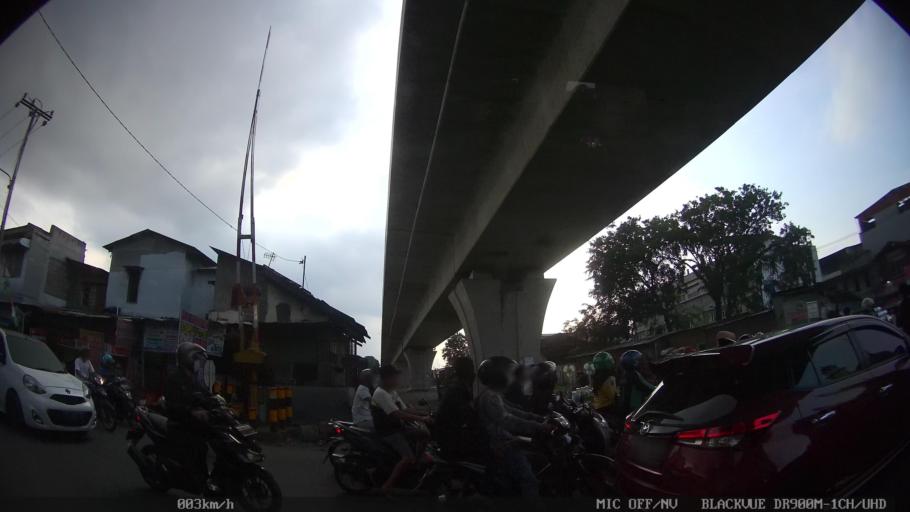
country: ID
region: North Sumatra
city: Medan
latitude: 3.5892
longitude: 98.7115
